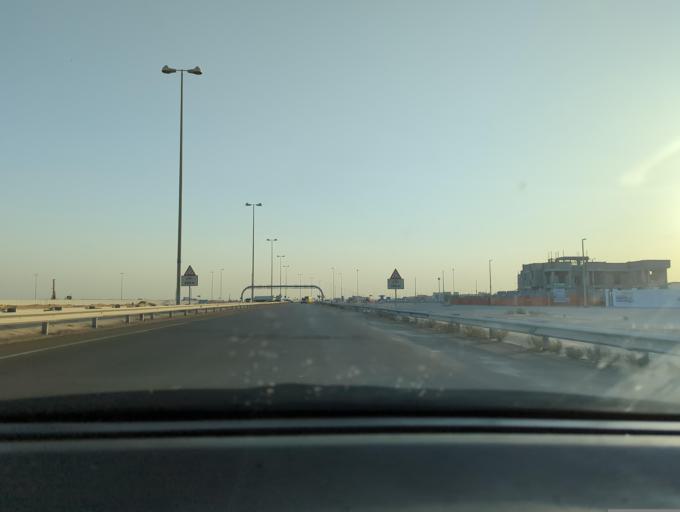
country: AE
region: Abu Dhabi
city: Abu Dhabi
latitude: 24.3630
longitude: 54.6685
